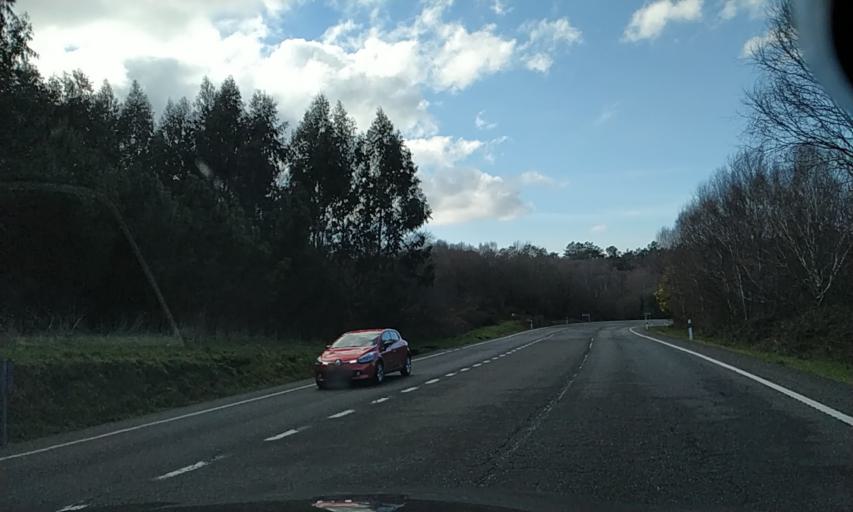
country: ES
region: Galicia
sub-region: Provincia da Coruna
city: Ribeira
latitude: 42.7108
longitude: -8.3555
